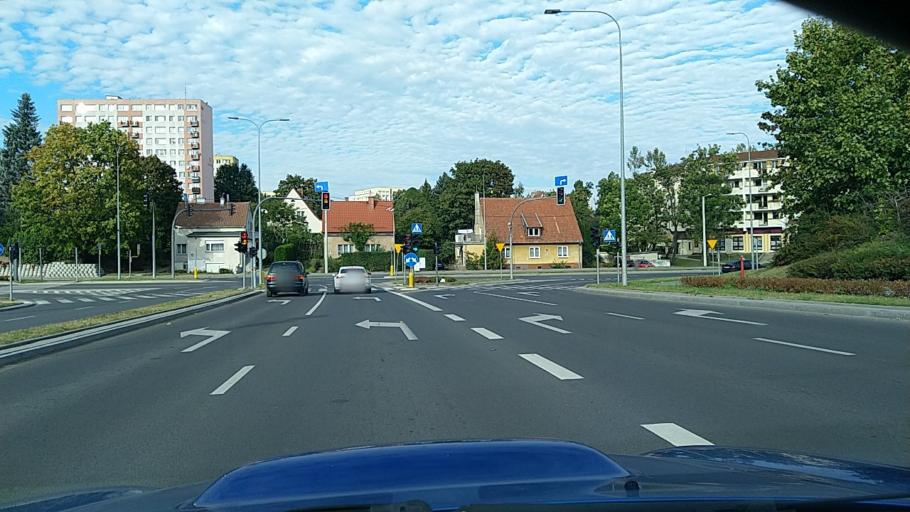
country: PL
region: Warmian-Masurian Voivodeship
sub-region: Powiat olsztynski
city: Olsztyn
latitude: 53.7740
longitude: 20.4943
